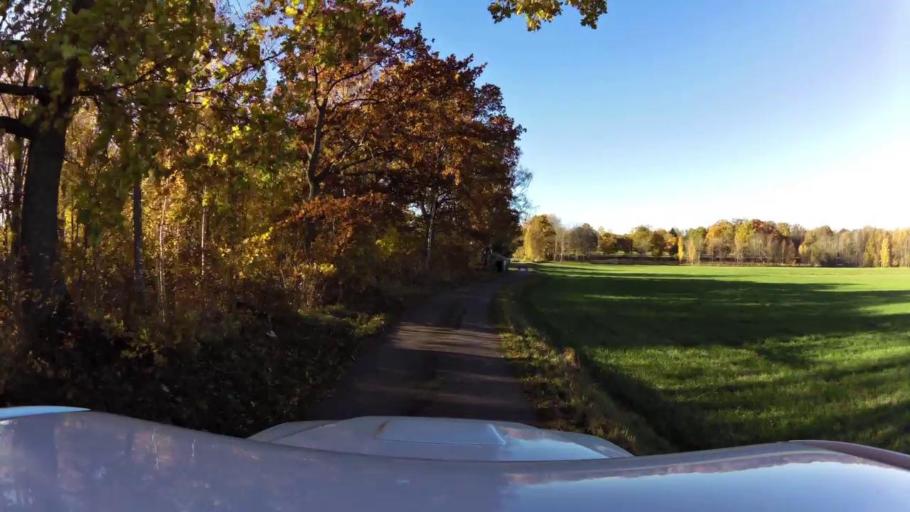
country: SE
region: OEstergoetland
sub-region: Linkopings Kommun
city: Ljungsbro
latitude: 58.5385
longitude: 15.3917
